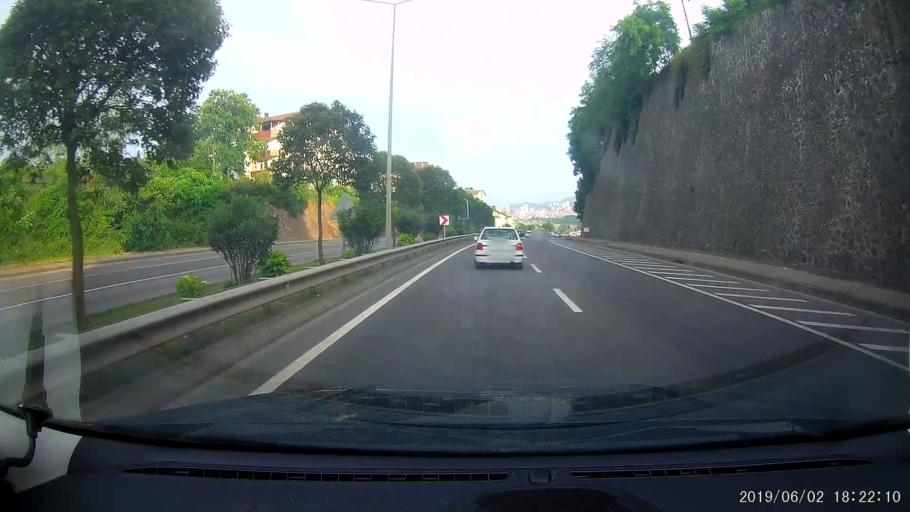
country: TR
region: Ordu
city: Fatsa
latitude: 41.0603
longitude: 37.4757
